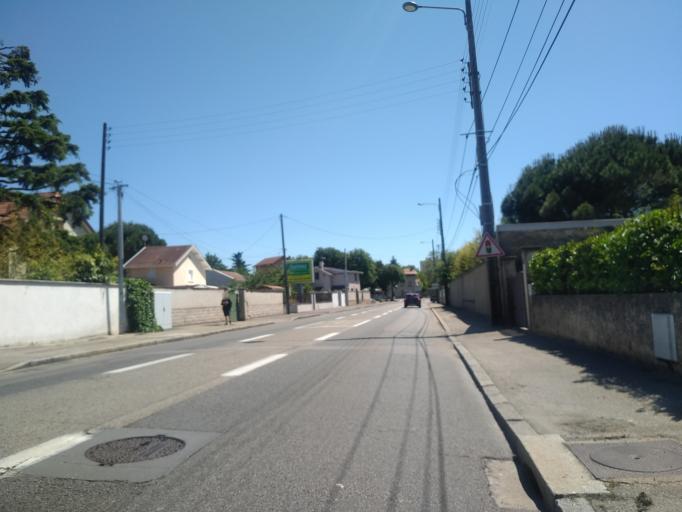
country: FR
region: Rhone-Alpes
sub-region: Departement du Rhone
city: Sathonay-Camp
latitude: 45.8171
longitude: 4.8629
